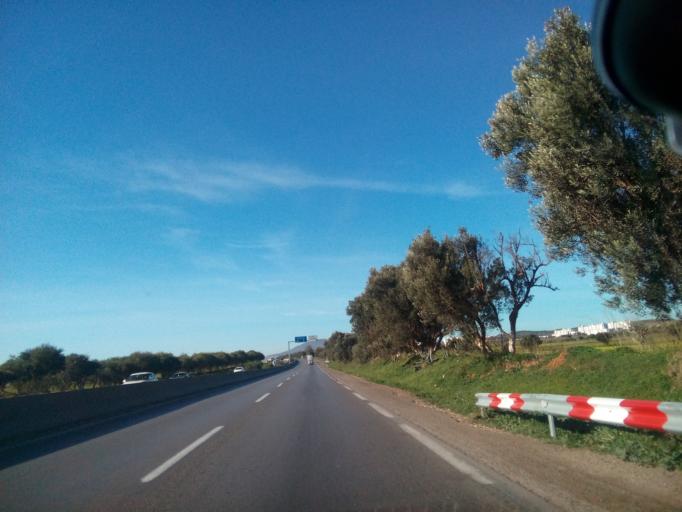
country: DZ
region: Oran
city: Ain el Bya
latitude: 35.7914
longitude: -0.4011
